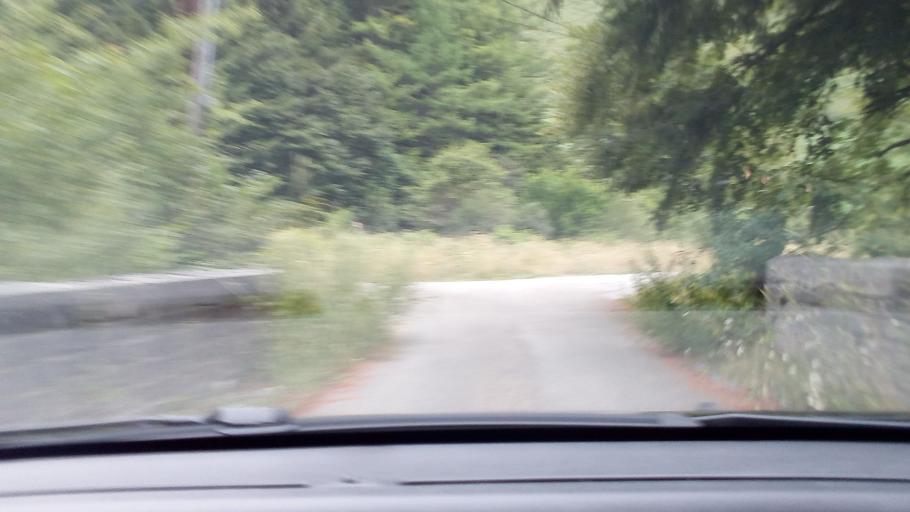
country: ES
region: Aragon
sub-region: Provincia de Huesca
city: Canfranc
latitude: 42.8192
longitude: -0.5616
